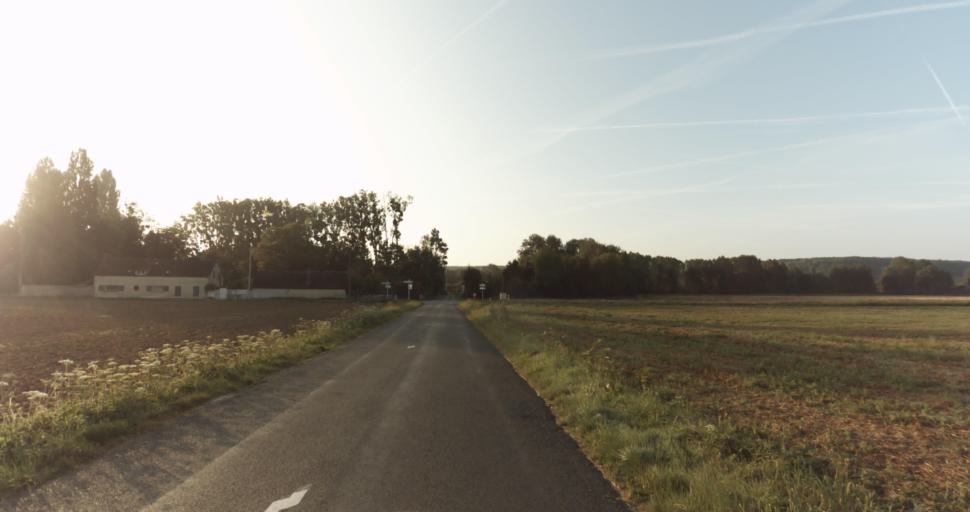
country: FR
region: Haute-Normandie
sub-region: Departement de l'Eure
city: Marcilly-sur-Eure
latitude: 48.7799
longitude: 1.3401
